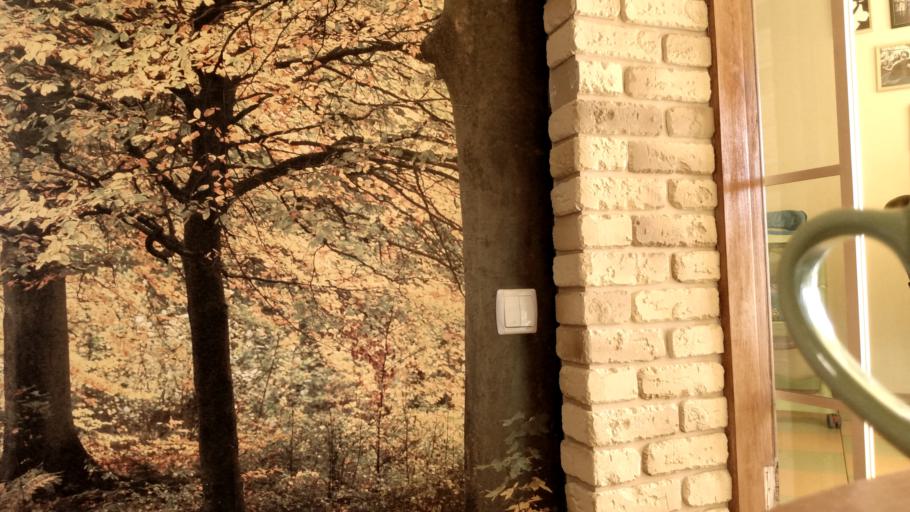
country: RU
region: Vologda
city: Imeni Zhelyabova
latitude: 58.8554
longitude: 36.8497
